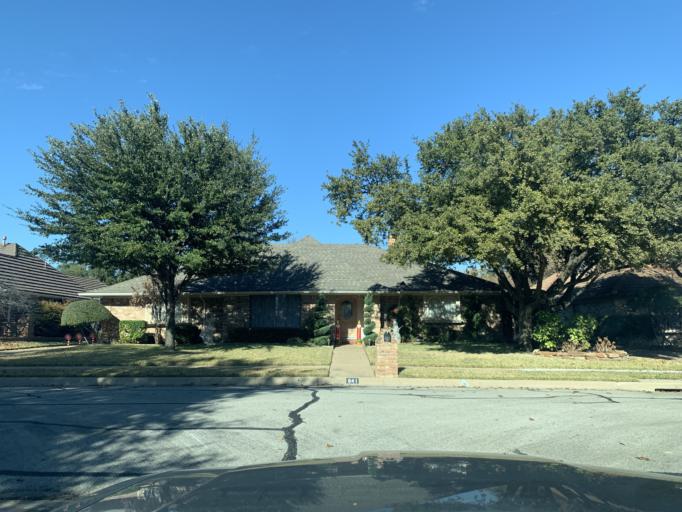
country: US
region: Texas
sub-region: Tarrant County
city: Bedford
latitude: 32.8452
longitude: -97.1549
